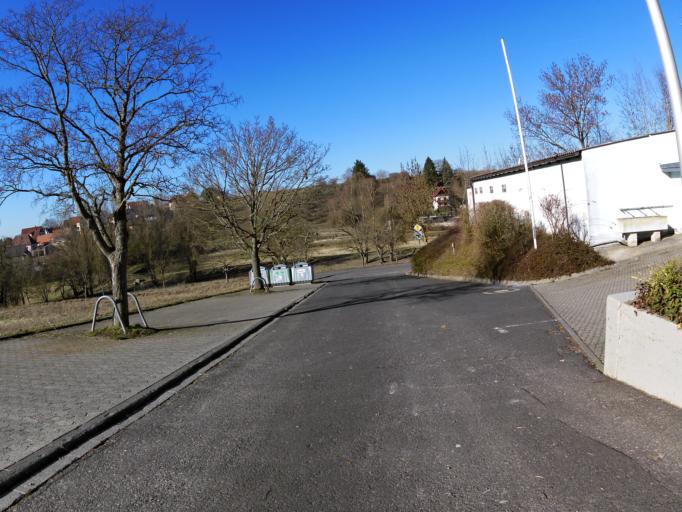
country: DE
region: Bavaria
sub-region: Regierungsbezirk Unterfranken
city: Rimpar
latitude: 49.8477
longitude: 9.9798
